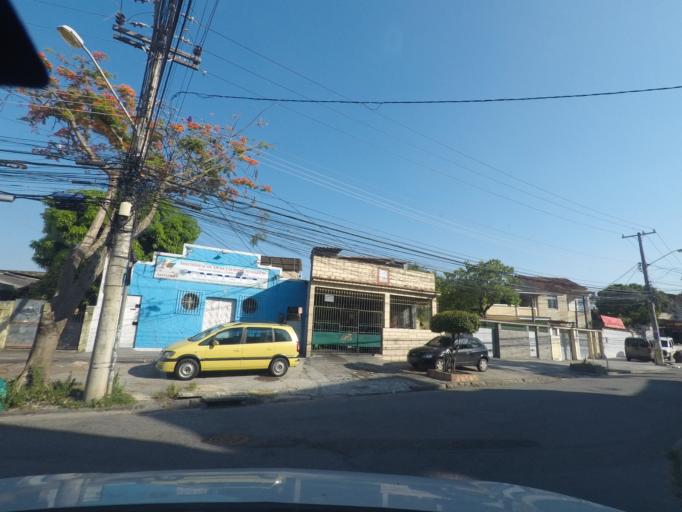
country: BR
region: Rio de Janeiro
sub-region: Duque De Caxias
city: Duque de Caxias
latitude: -22.8281
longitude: -43.2850
